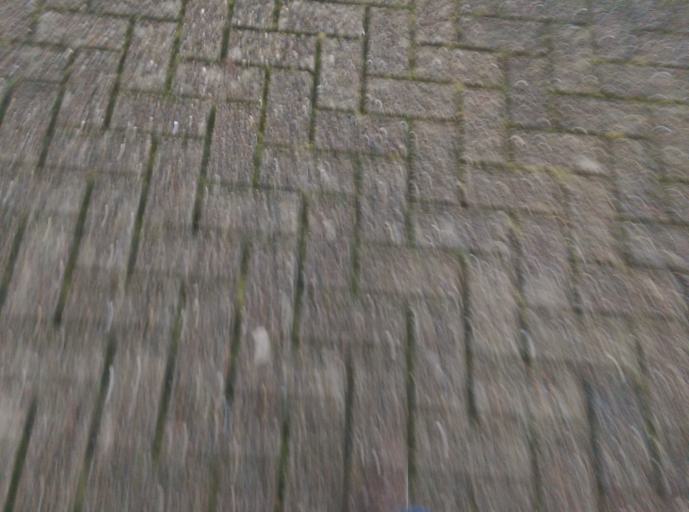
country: DE
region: Lower Saxony
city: Oldenburg
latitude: 53.1611
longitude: 8.2045
